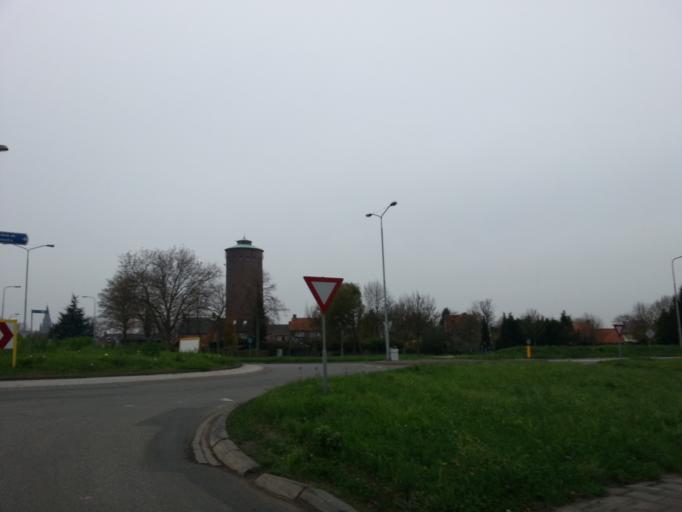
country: NL
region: North Brabant
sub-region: Gemeente Steenbergen
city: Welberg
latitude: 51.5886
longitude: 4.3328
